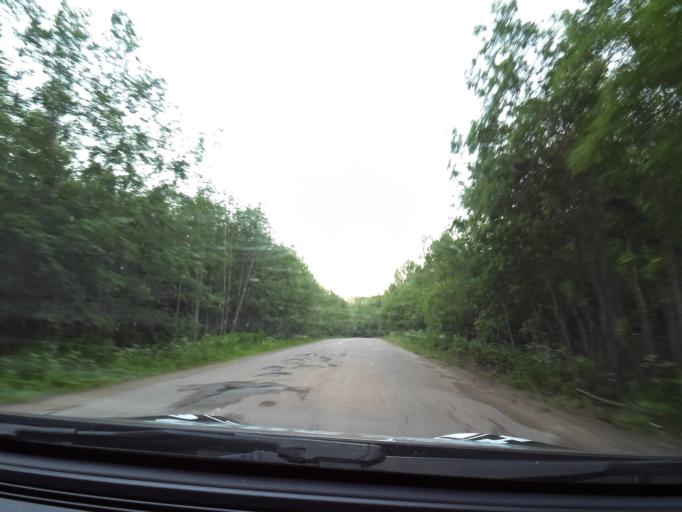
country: RU
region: Leningrad
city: Voznesen'ye
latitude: 60.9537
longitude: 35.4705
